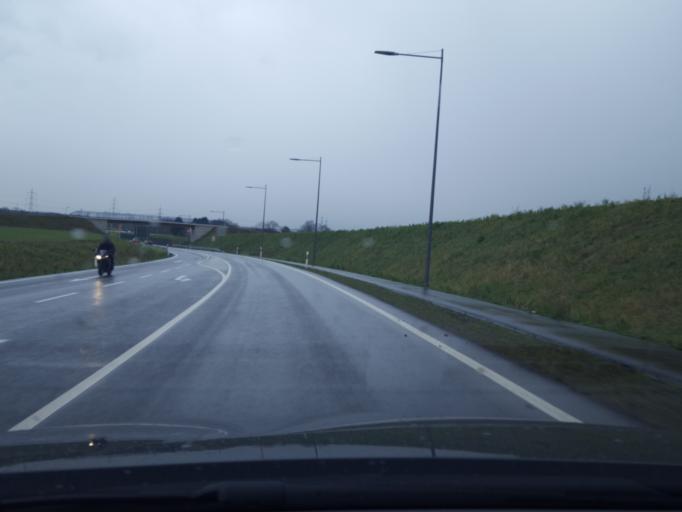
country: DE
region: North Rhine-Westphalia
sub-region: Regierungsbezirk Koln
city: Troisdorf
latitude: 50.7995
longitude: 7.1107
